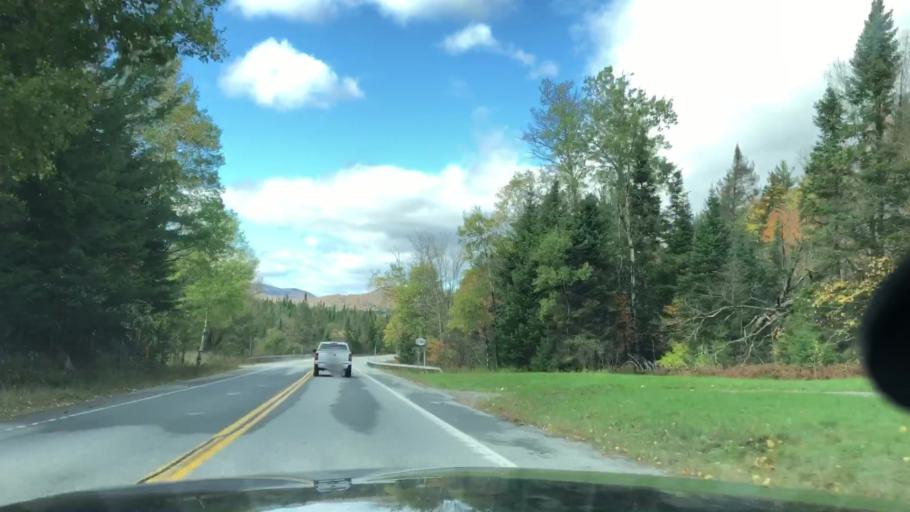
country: US
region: New York
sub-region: Essex County
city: Lake Placid
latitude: 43.8710
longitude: -74.0011
